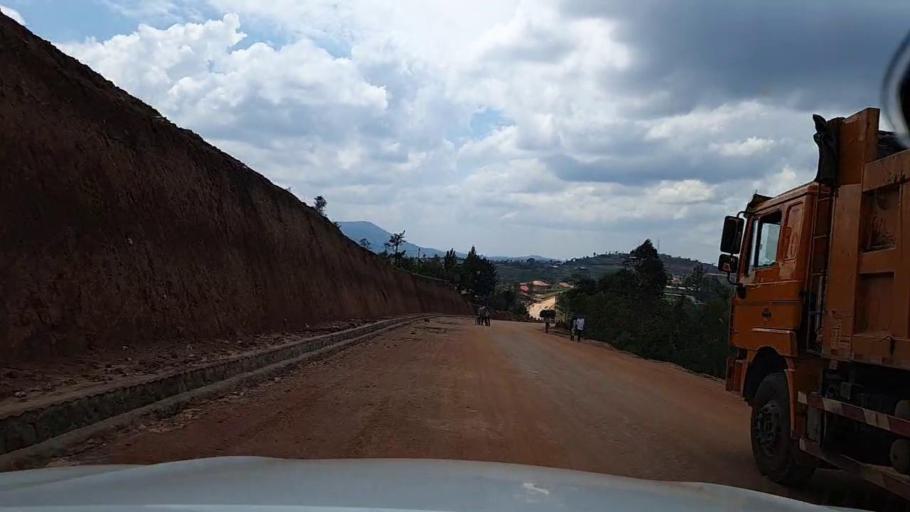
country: RW
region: Southern Province
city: Butare
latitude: -2.6881
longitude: 29.5653
